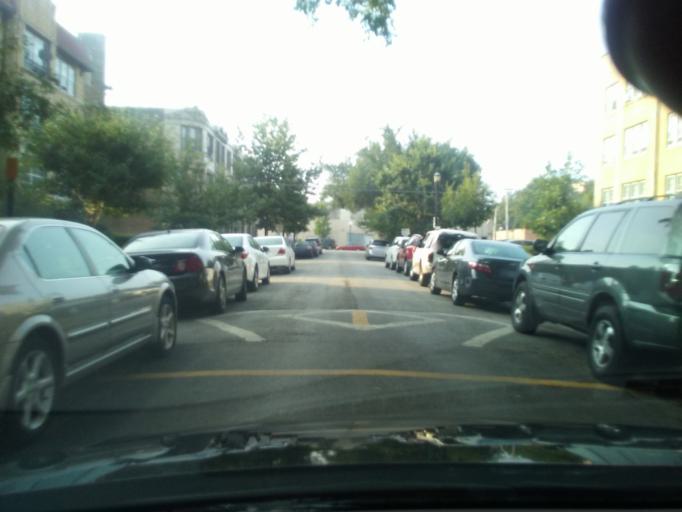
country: US
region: Illinois
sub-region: Cook County
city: Evanston
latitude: 42.0202
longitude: -87.6780
